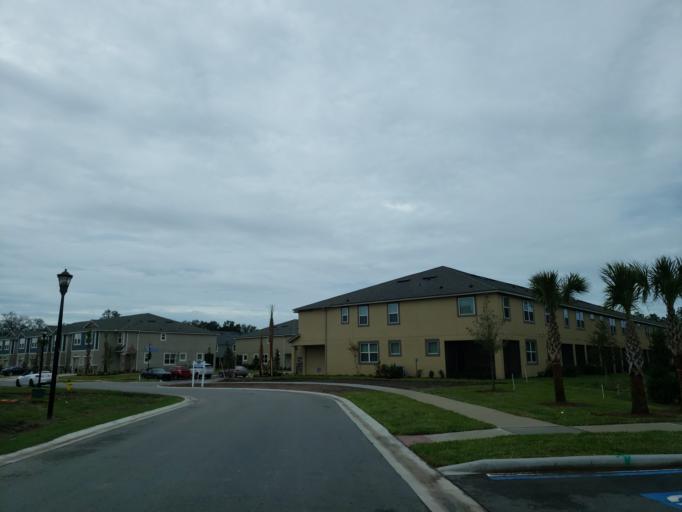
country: US
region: Florida
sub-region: Hillsborough County
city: Riverview
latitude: 27.8514
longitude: -82.3064
